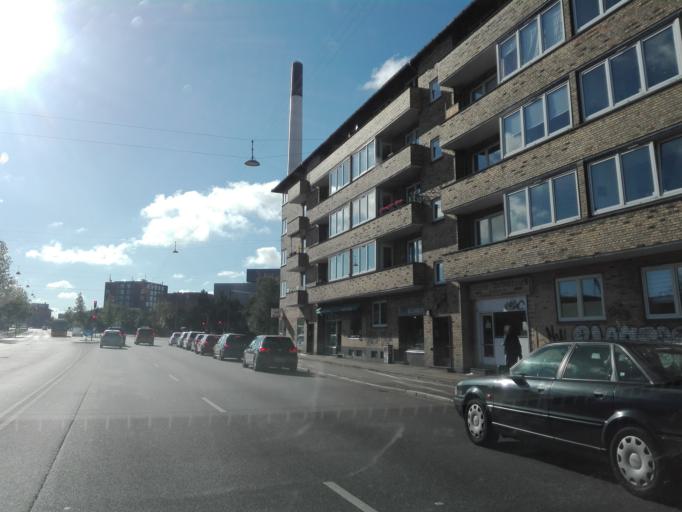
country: DK
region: Capital Region
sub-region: Frederiksberg Kommune
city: Frederiksberg
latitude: 55.7089
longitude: 12.5390
